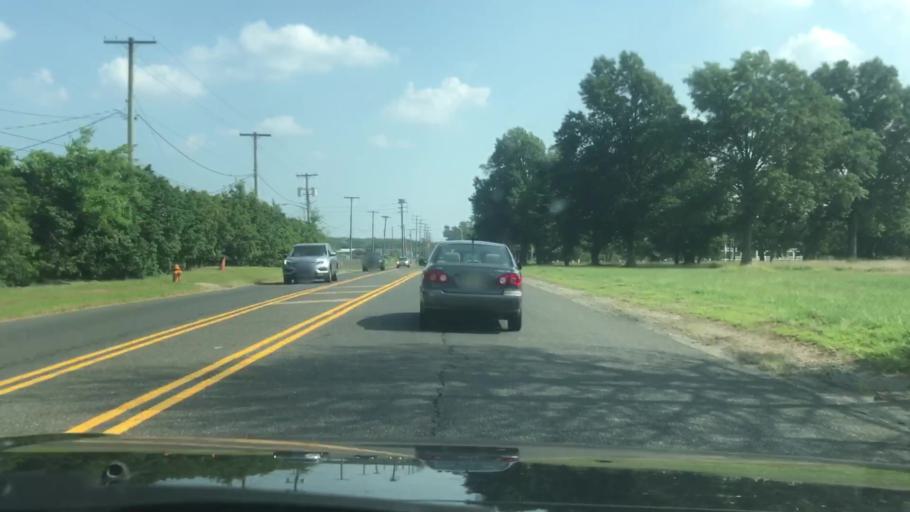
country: US
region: New Jersey
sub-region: Monmouth County
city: Oceanport
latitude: 40.3200
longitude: -74.0354
